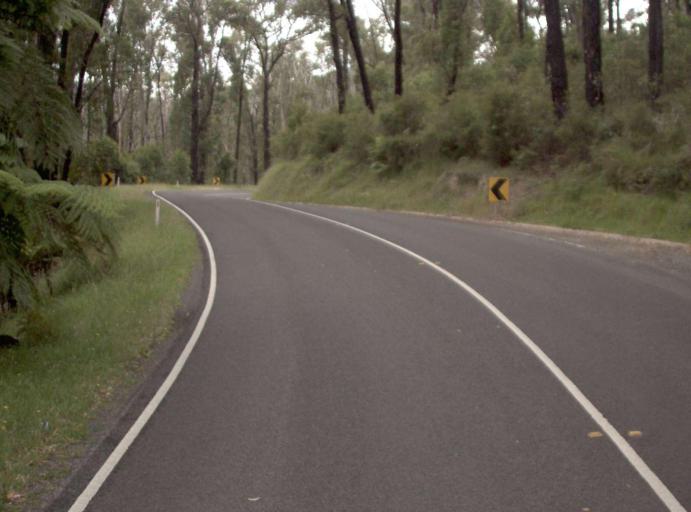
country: AU
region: Victoria
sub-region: Yarra Ranges
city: Healesville
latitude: -37.6313
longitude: 145.5917
